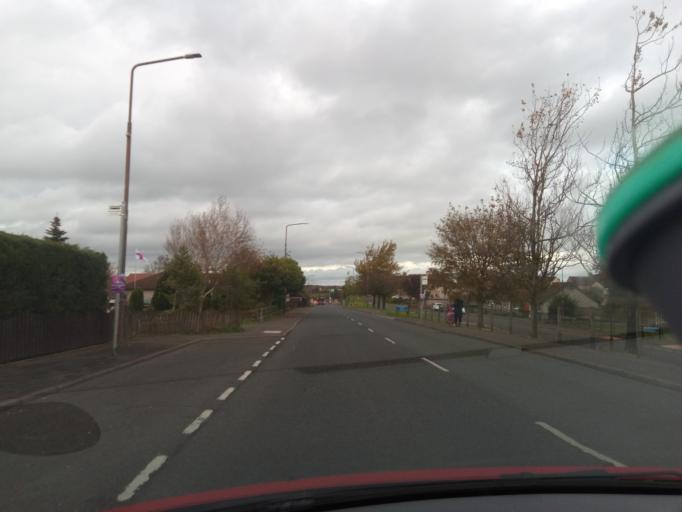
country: GB
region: Scotland
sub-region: West Lothian
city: Blackburn
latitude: 55.8422
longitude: -3.6157
